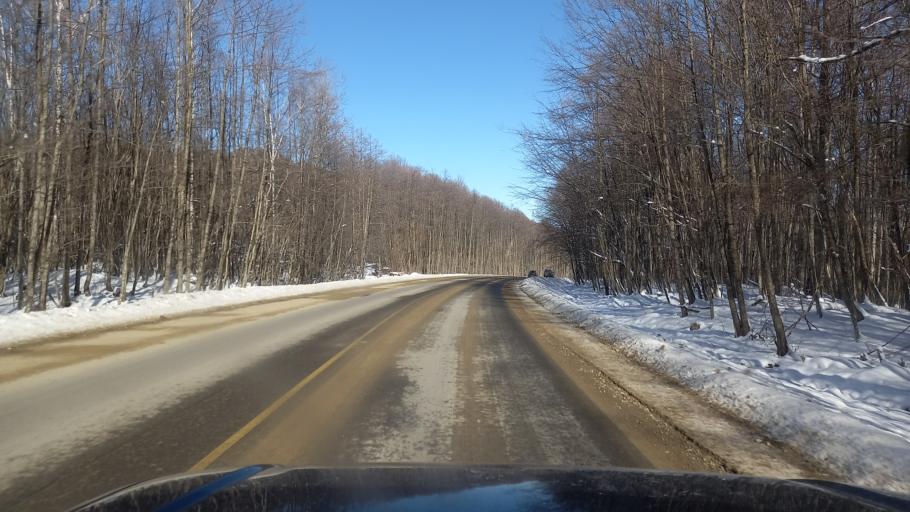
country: RU
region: Adygeya
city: Kamennomostskiy
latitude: 44.2148
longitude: 40.0768
